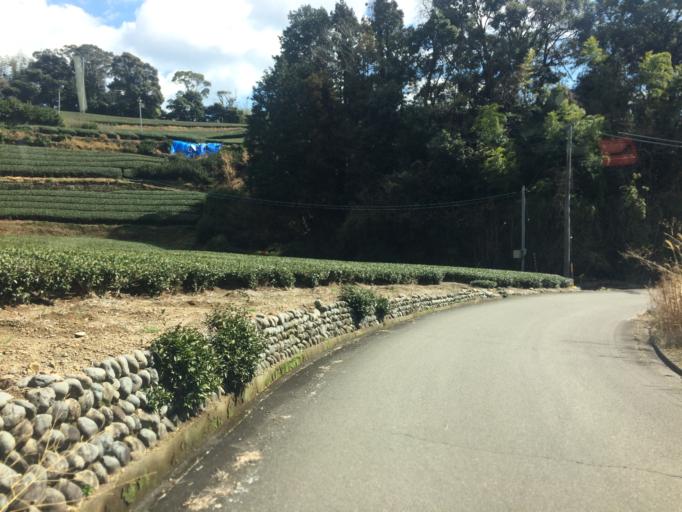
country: JP
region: Shizuoka
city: Shimada
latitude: 34.7654
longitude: 138.1980
